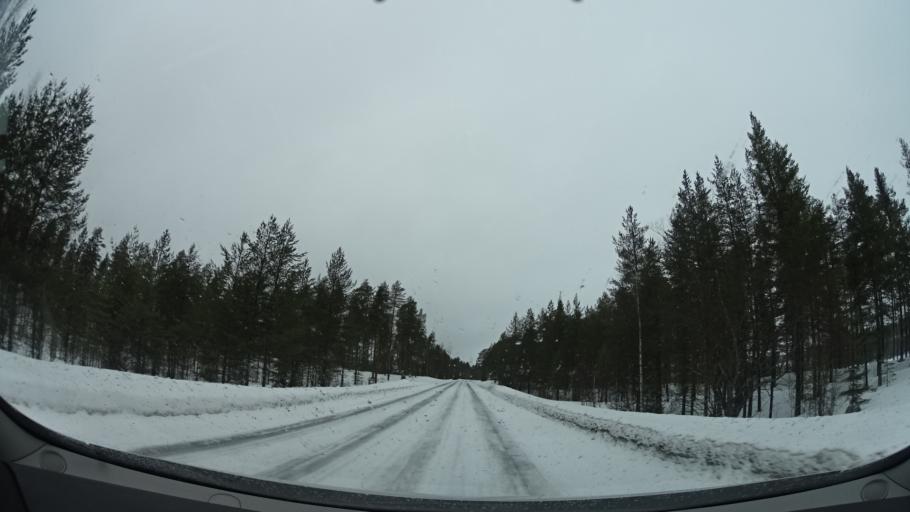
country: SE
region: Vaesterbotten
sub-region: Mala Kommun
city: Mala
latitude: 65.1491
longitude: 18.8145
